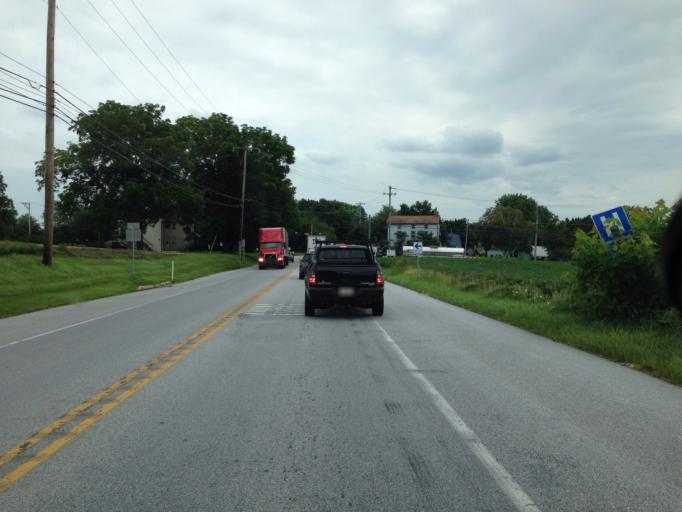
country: US
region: Pennsylvania
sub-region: Chester County
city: Oxford
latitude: 39.8180
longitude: -75.9121
